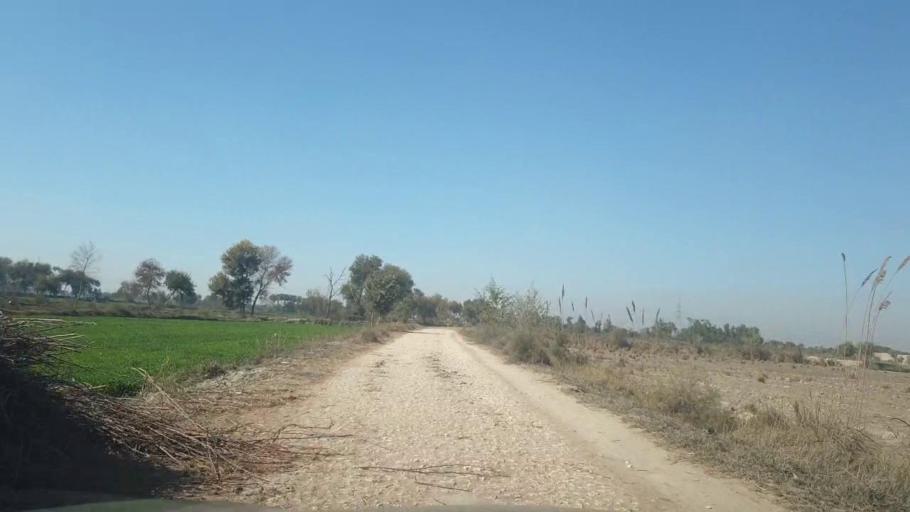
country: PK
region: Sindh
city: Adilpur
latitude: 27.8930
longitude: 69.2808
